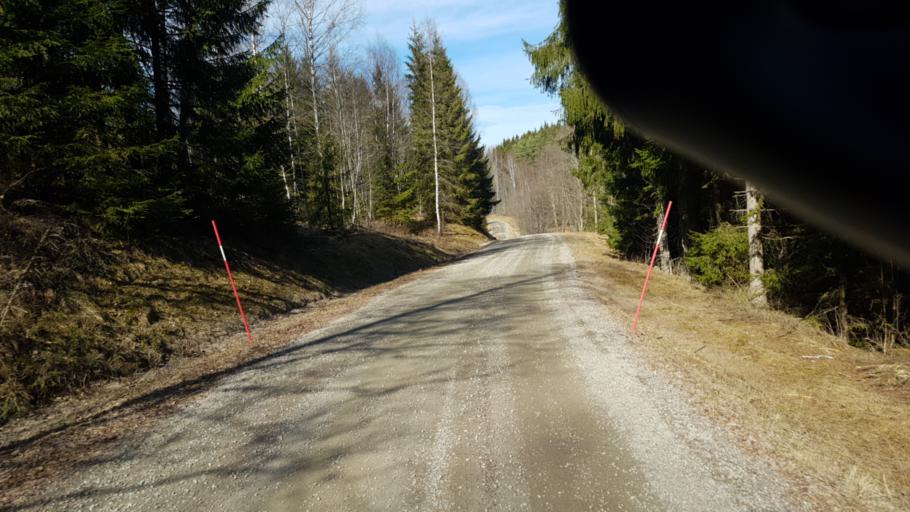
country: SE
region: Vaermland
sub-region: Arvika Kommun
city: Arvika
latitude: 59.6818
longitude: 12.7707
